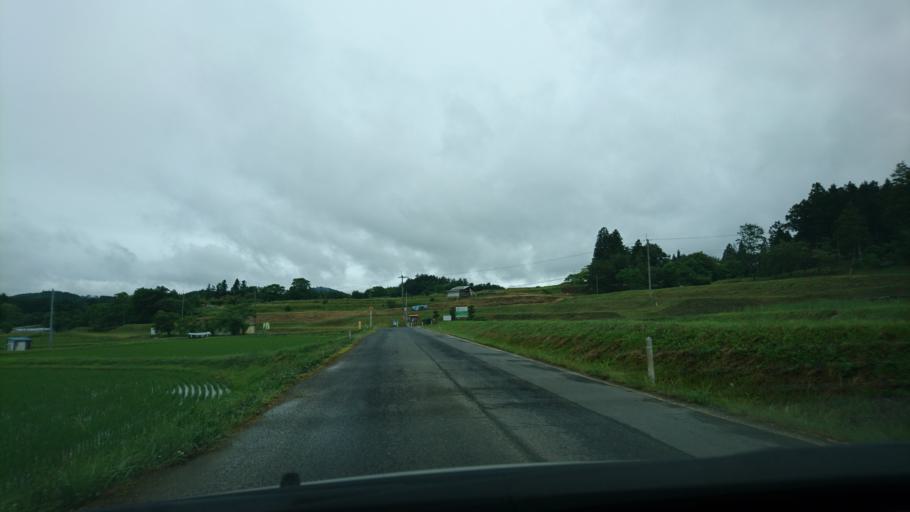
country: JP
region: Iwate
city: Ichinoseki
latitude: 38.9246
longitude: 141.2093
